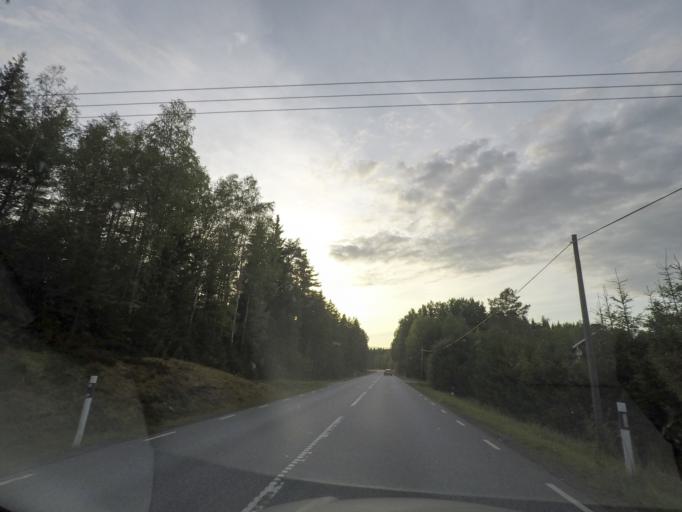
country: SE
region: OErebro
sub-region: Nora Kommun
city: As
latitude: 59.5204
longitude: 14.9041
